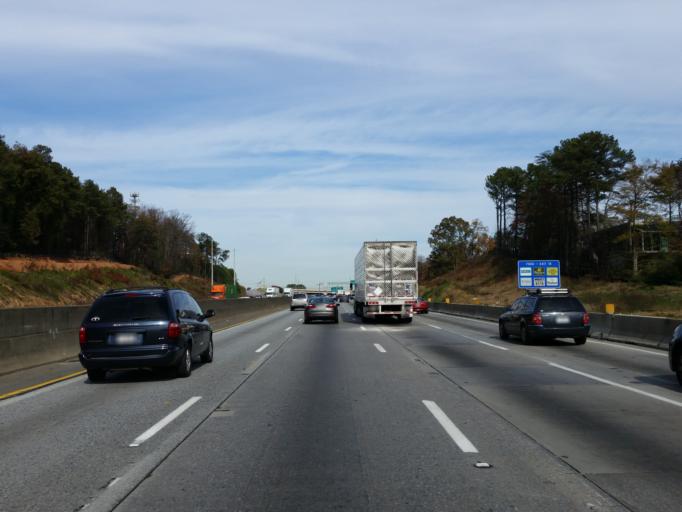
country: US
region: Georgia
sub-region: Cobb County
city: Vinings
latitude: 33.8571
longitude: -84.4824
